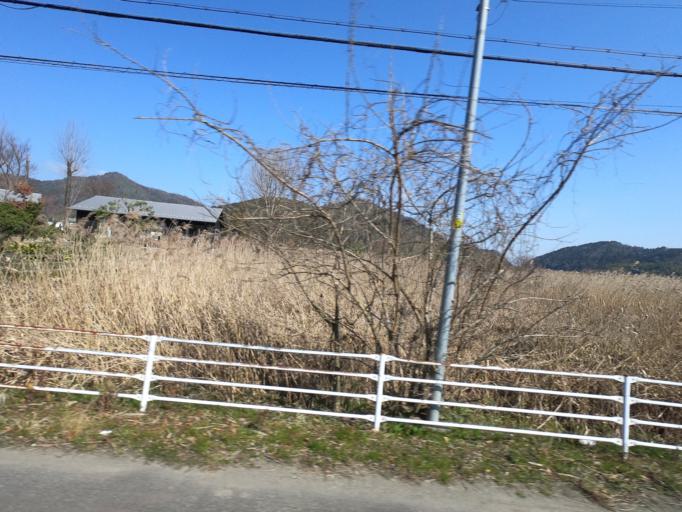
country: JP
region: Shiga Prefecture
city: Omihachiman
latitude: 35.1439
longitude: 136.0518
